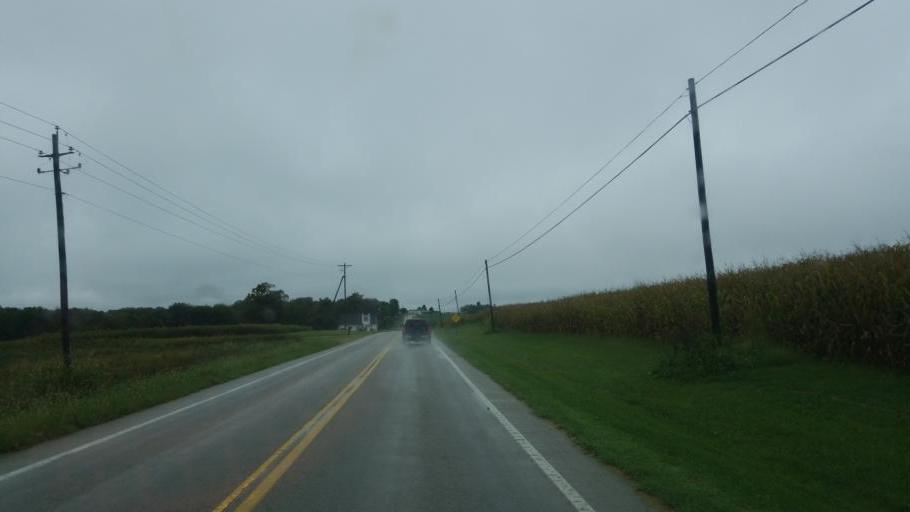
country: US
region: Ohio
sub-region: Adams County
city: West Union
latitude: 38.8005
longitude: -83.4799
